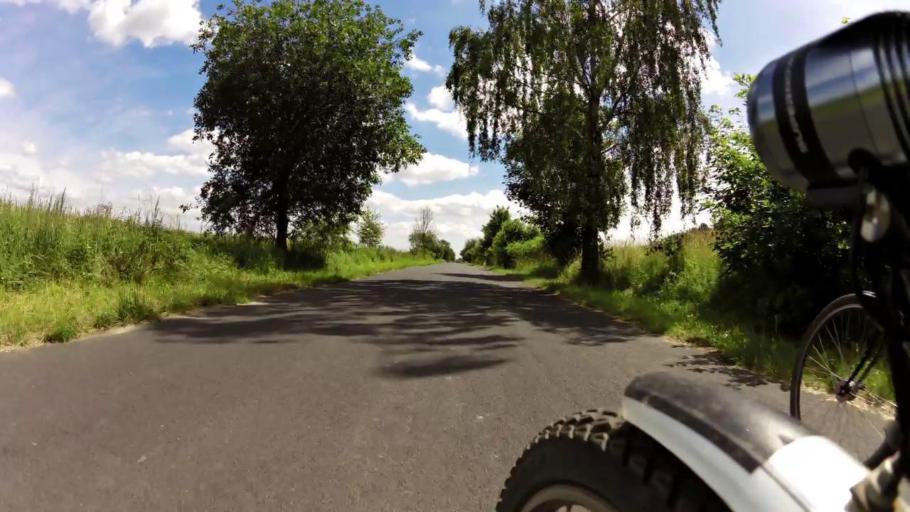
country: PL
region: West Pomeranian Voivodeship
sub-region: Powiat choszczenski
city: Choszczno
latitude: 53.2269
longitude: 15.4160
